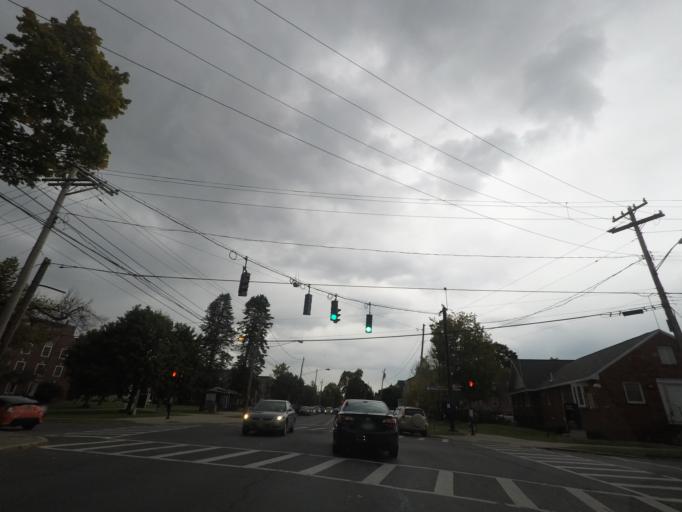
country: US
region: New York
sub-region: Albany County
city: West Albany
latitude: 42.6636
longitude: -73.7826
